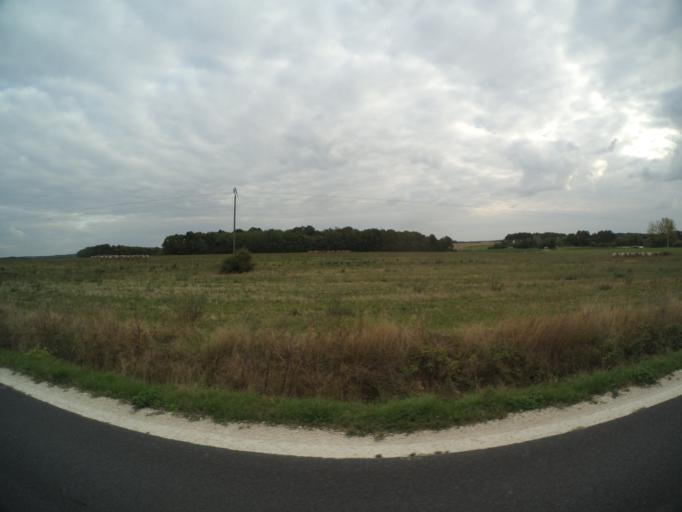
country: FR
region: Centre
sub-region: Departement d'Indre-et-Loire
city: Nazelles-Negron
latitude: 47.4897
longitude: 0.9545
